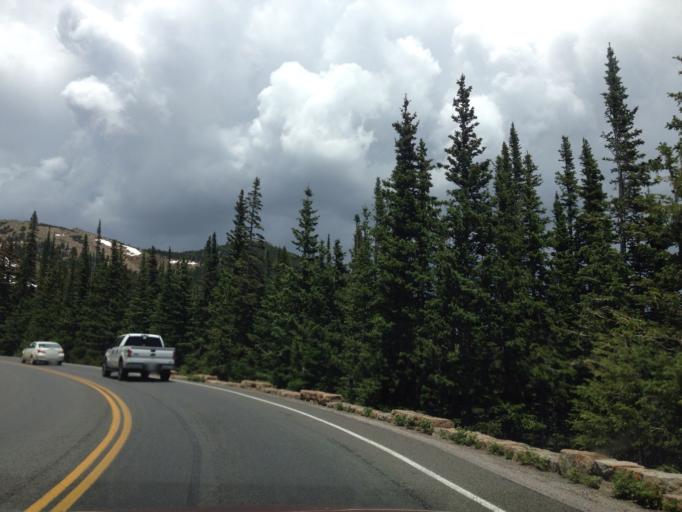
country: US
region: Colorado
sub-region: Larimer County
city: Estes Park
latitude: 40.3870
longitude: -105.6681
